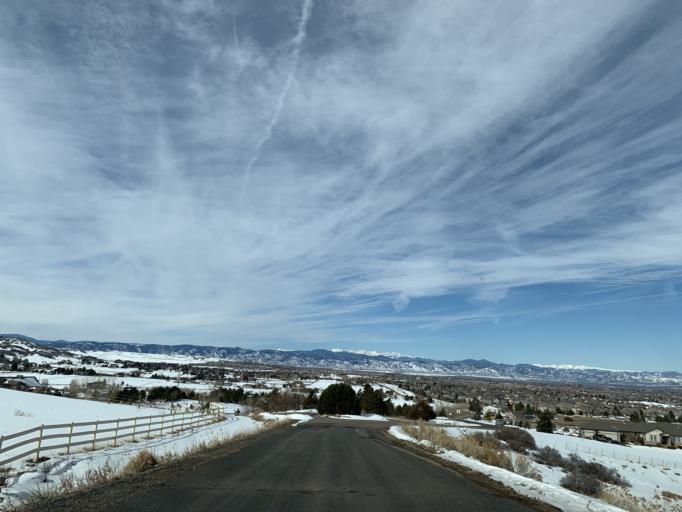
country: US
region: Colorado
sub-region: Douglas County
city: Carriage Club
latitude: 39.5201
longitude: -104.8951
